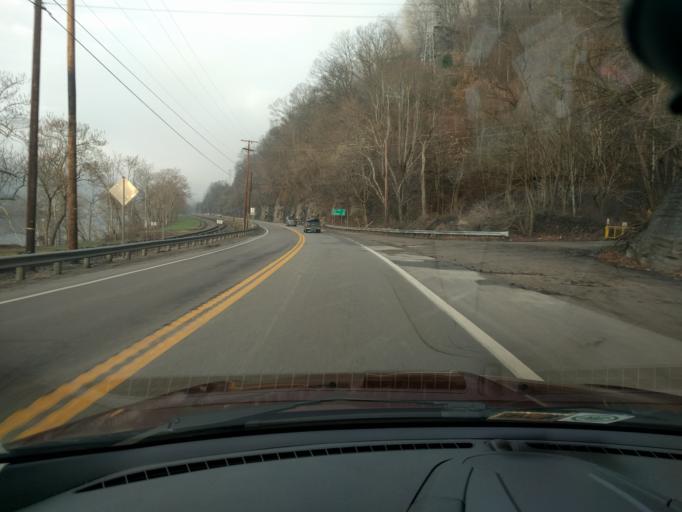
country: US
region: West Virginia
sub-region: Kanawha County
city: Montgomery
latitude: 38.1855
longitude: -81.3230
